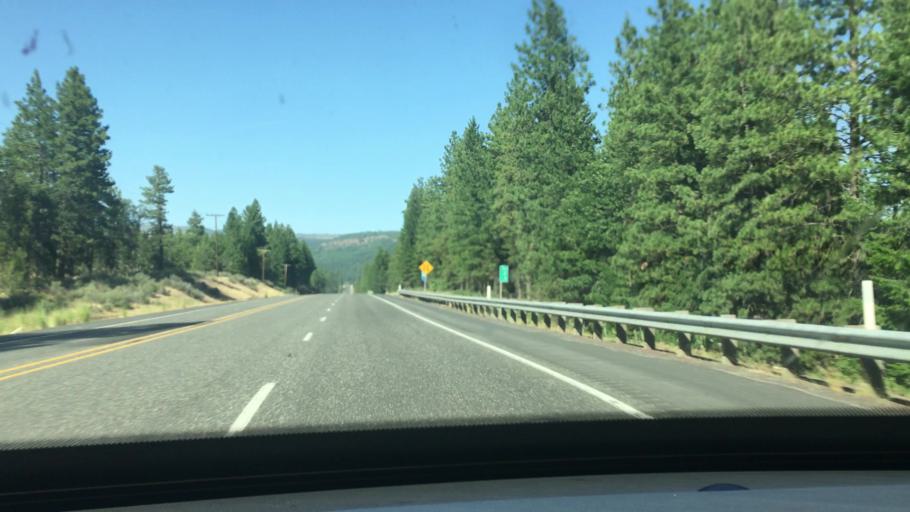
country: US
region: Washington
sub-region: Klickitat County
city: Goldendale
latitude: 45.9345
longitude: -120.6929
